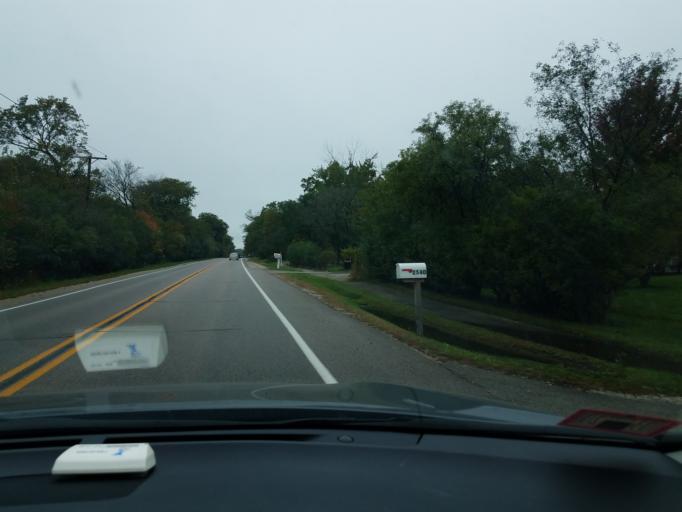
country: US
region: Illinois
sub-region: Lake County
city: Riverwoods
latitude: 42.1675
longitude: -87.8892
